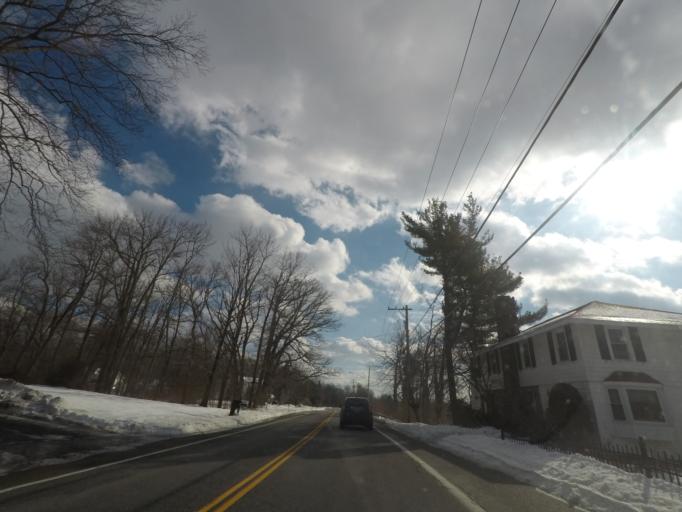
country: US
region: New York
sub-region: Schenectady County
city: East Glenville
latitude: 42.8526
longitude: -73.8813
